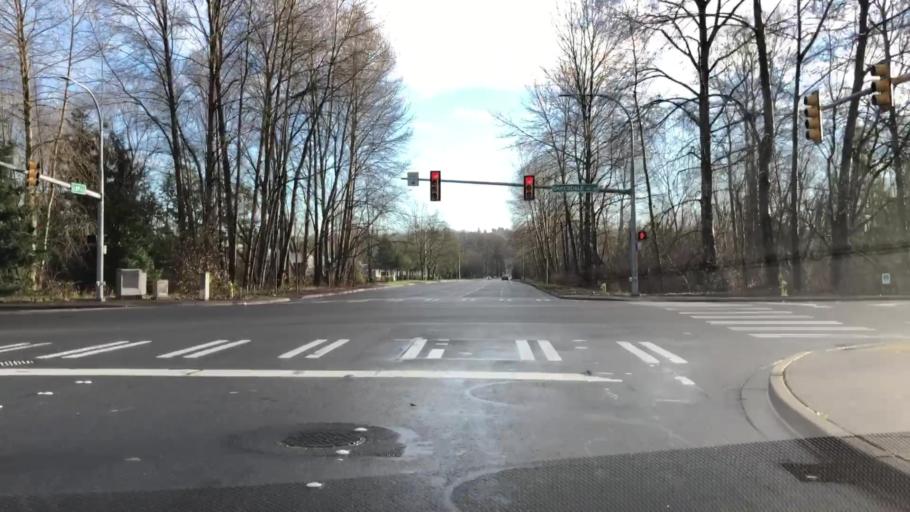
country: US
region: Washington
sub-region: King County
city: Renton
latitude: 47.4556
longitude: -122.2331
